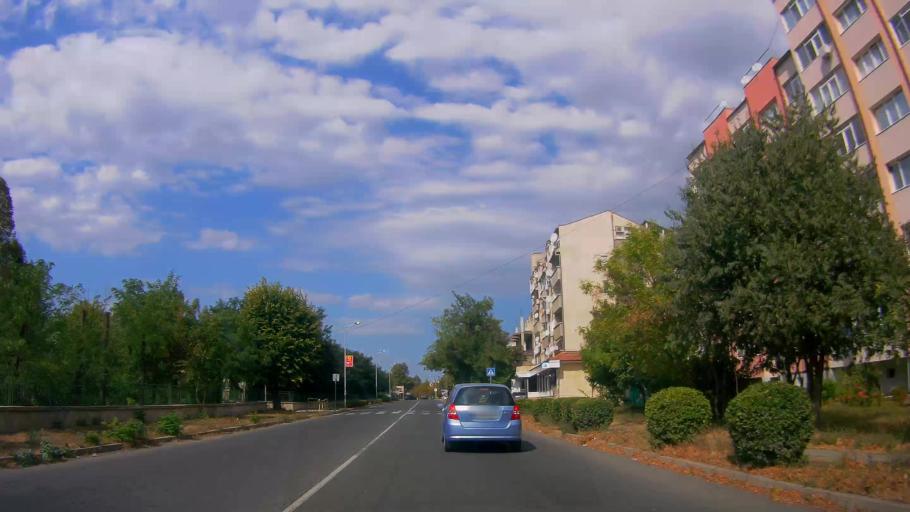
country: BG
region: Burgas
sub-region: Obshtina Aytos
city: Aytos
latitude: 42.6977
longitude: 27.2569
